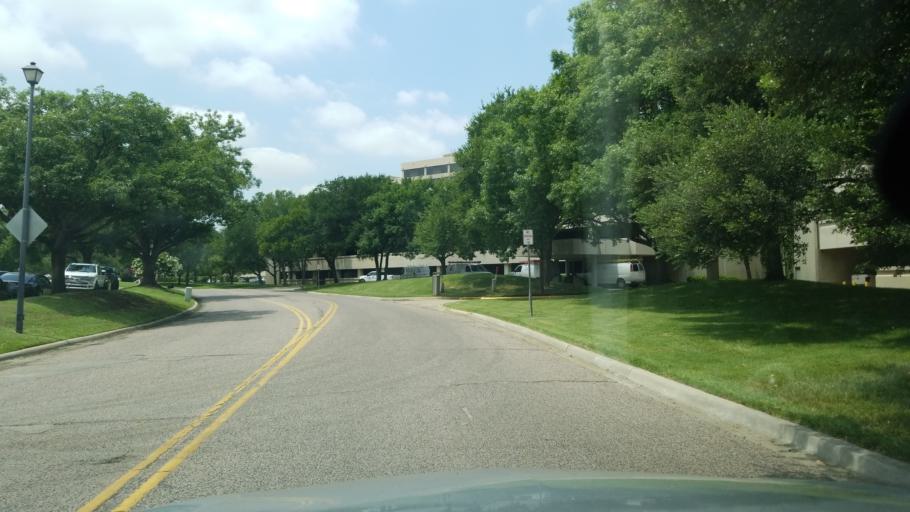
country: US
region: Texas
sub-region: Dallas County
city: Irving
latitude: 32.8612
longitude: -96.9392
